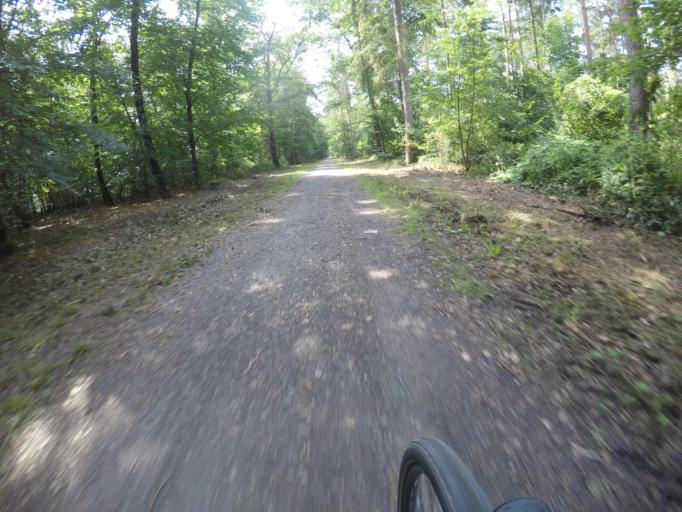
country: DE
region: Baden-Wuerttemberg
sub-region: Karlsruhe Region
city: Reilingen
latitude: 49.2813
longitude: 8.5707
